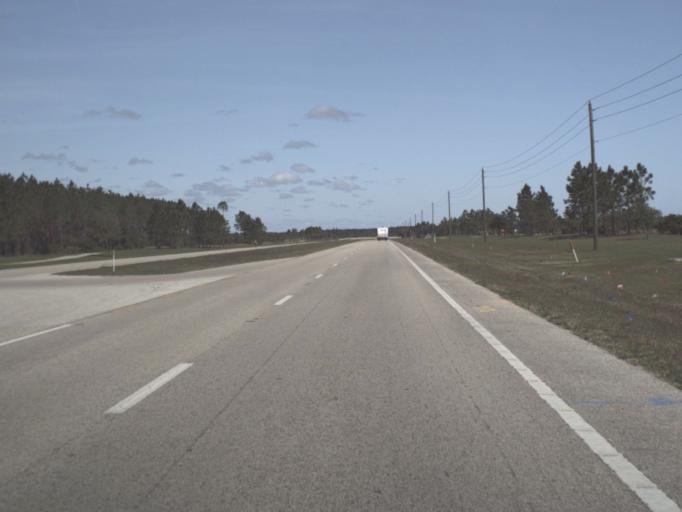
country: US
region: Florida
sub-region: Flagler County
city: Palm Coast
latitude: 29.5923
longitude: -81.2811
